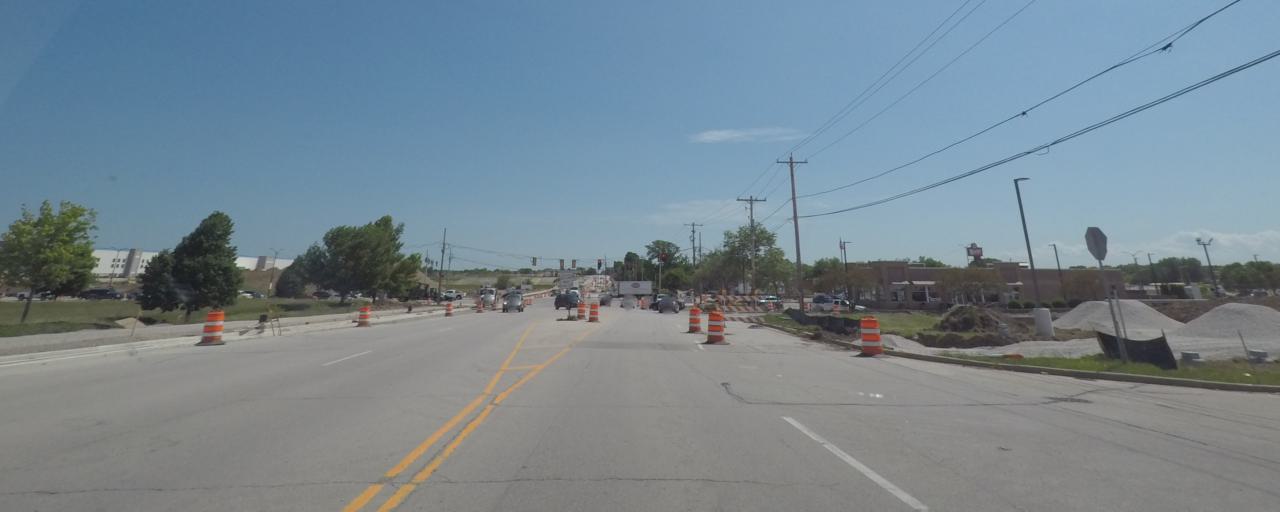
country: US
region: Wisconsin
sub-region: Racine County
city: Caledonia
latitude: 42.8738
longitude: -87.9323
